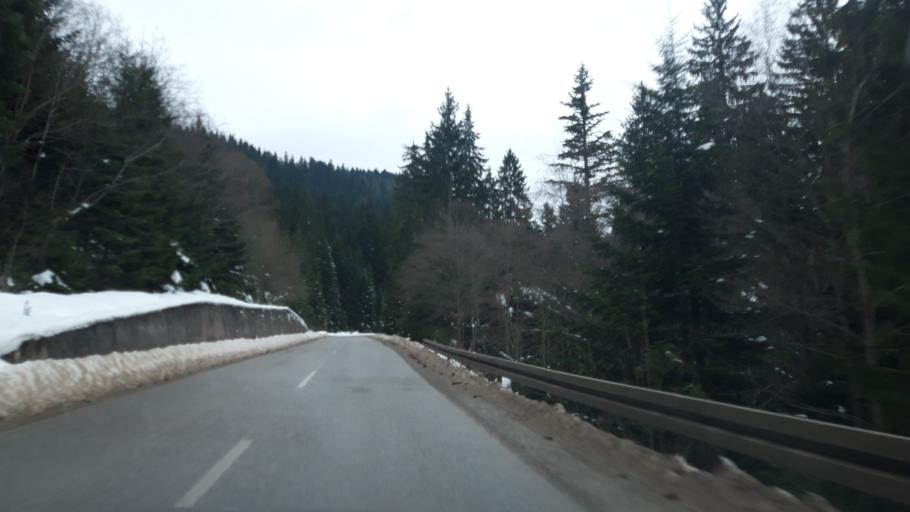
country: BA
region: Republika Srpska
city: Koran
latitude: 43.7772
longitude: 18.5532
